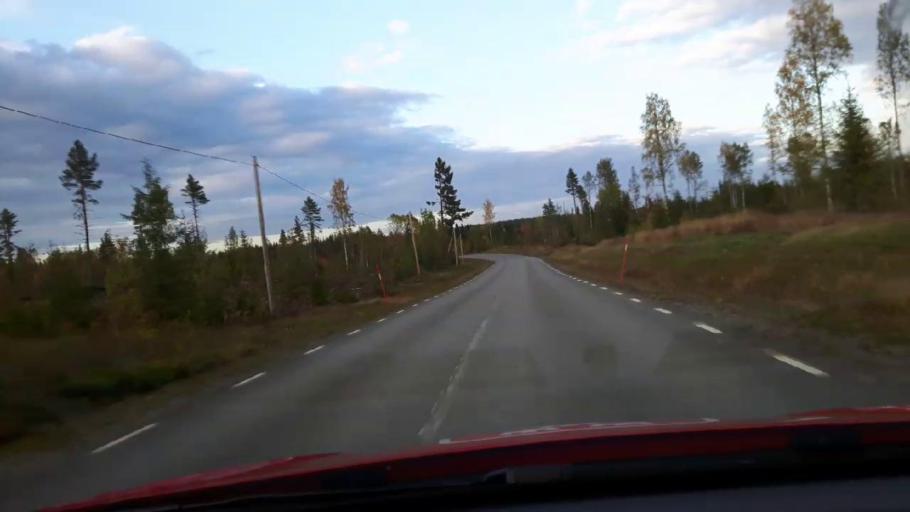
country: SE
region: Jaemtland
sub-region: OEstersunds Kommun
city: Lit
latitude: 63.3187
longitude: 15.1476
